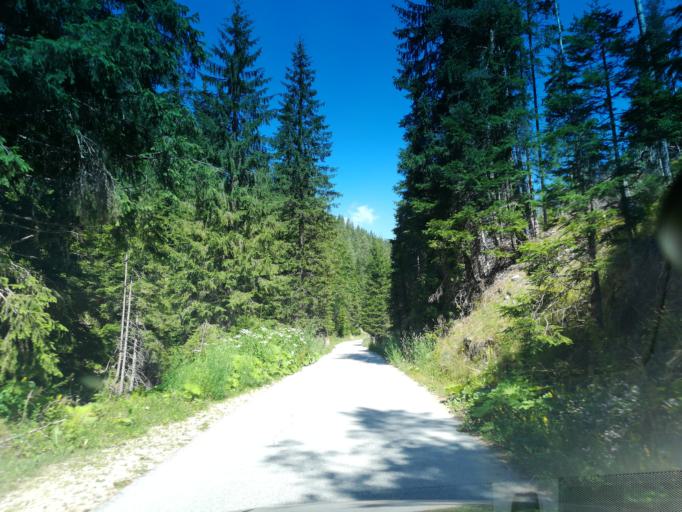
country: BG
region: Smolyan
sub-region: Obshtina Smolyan
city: Smolyan
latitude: 41.6610
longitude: 24.8052
